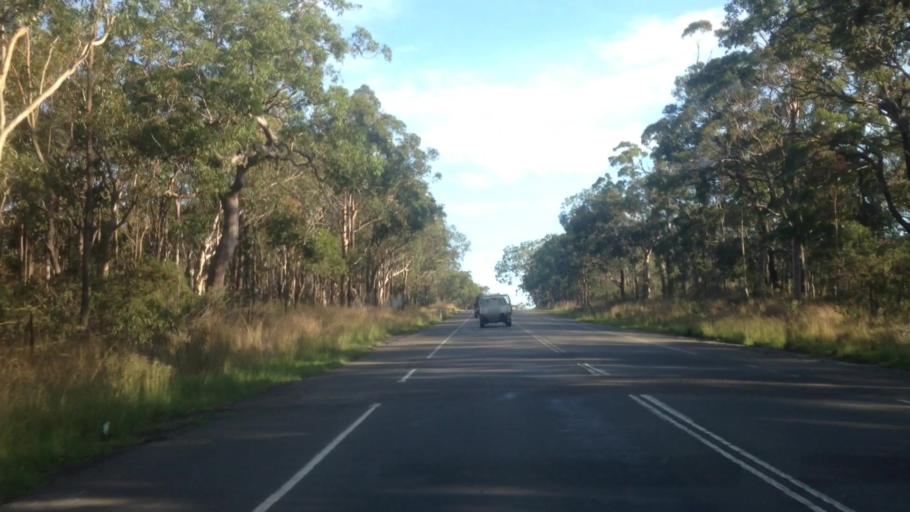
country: AU
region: New South Wales
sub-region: Lake Macquarie Shire
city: Dora Creek
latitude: -33.1270
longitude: 151.4757
